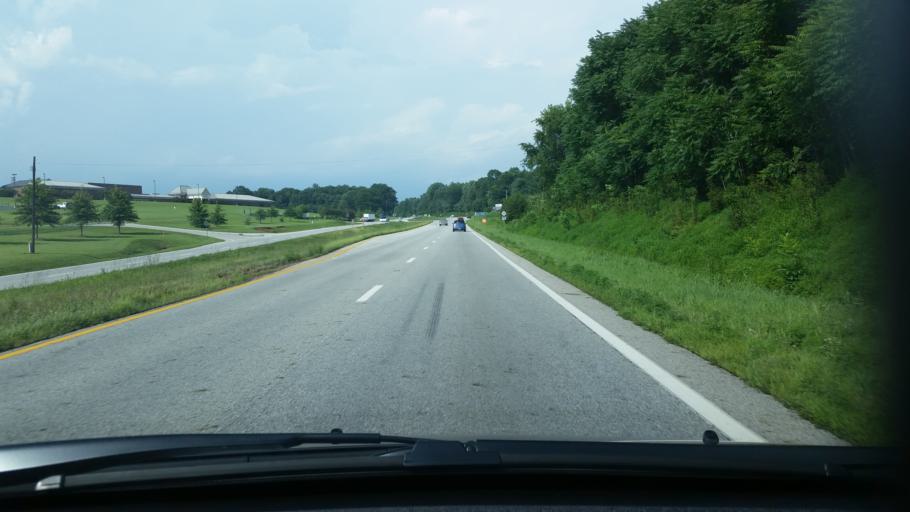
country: US
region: Virginia
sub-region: Nelson County
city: Lovingston
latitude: 37.7294
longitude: -78.8960
